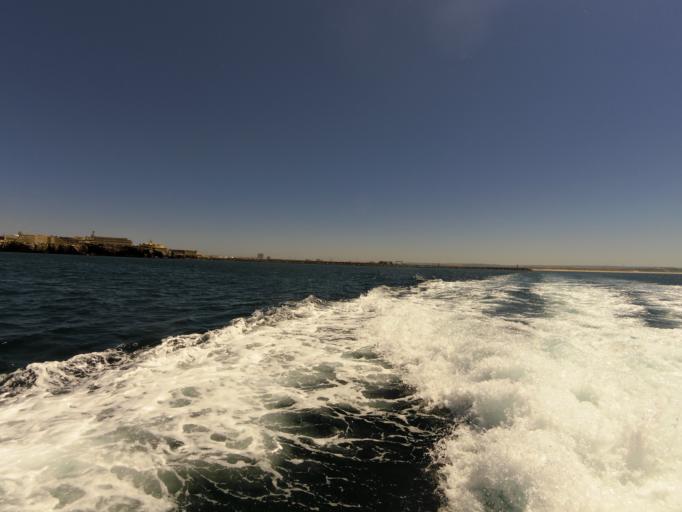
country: PT
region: Leiria
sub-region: Peniche
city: Peniche
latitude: 39.3492
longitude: -9.3849
